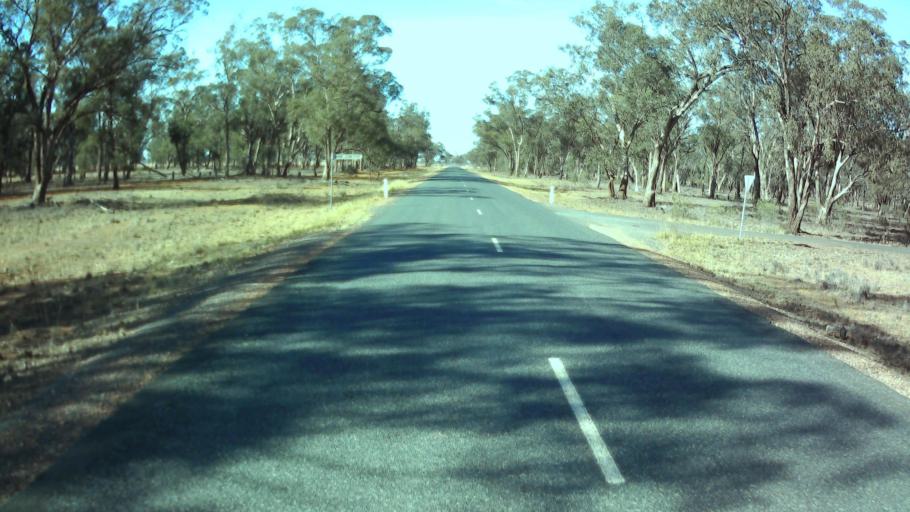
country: AU
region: New South Wales
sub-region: Weddin
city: Grenfell
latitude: -34.0645
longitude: 147.9078
